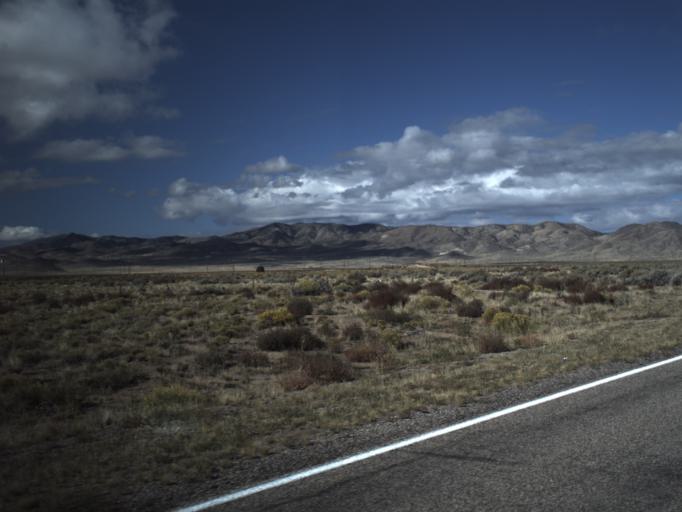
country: US
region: Utah
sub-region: Beaver County
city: Milford
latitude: 38.3989
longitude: -113.0302
